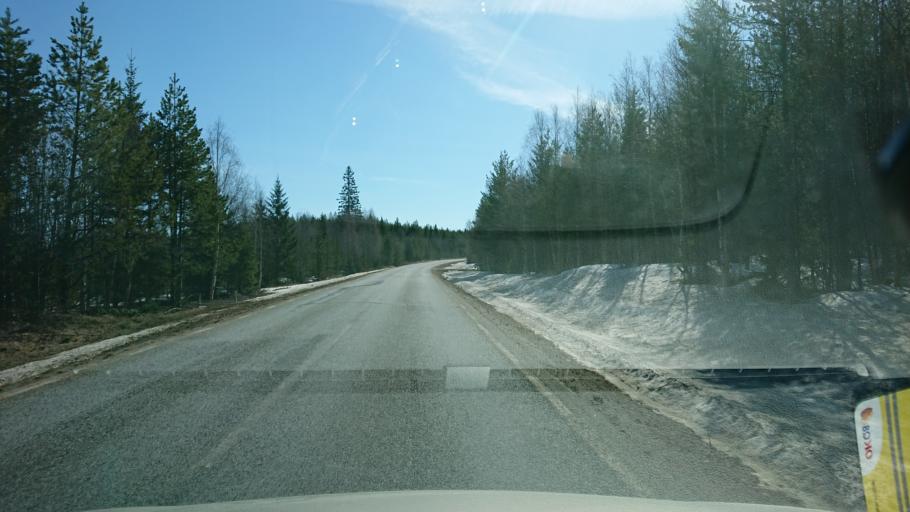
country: SE
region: Vaesterbotten
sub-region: Dorotea Kommun
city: Dorotea
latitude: 63.9954
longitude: 16.3105
